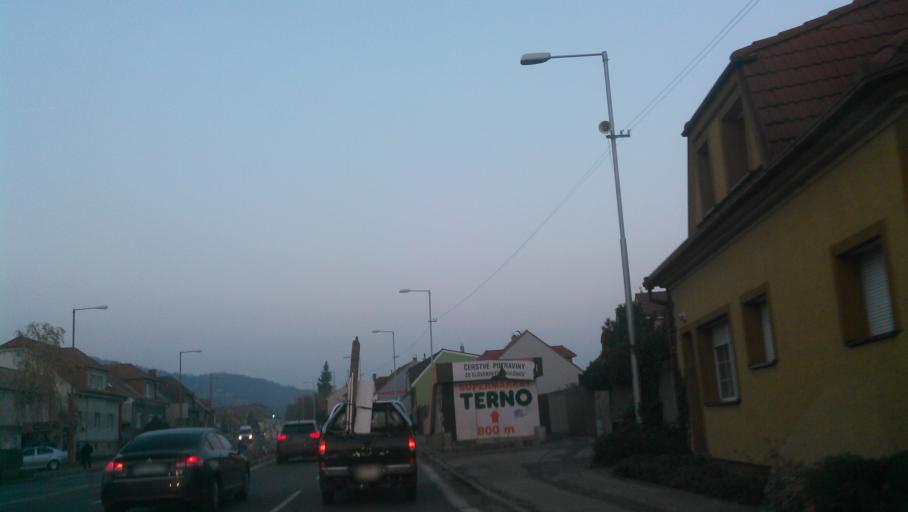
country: SK
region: Bratislavsky
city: Svaty Jur
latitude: 48.2491
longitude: 17.2127
